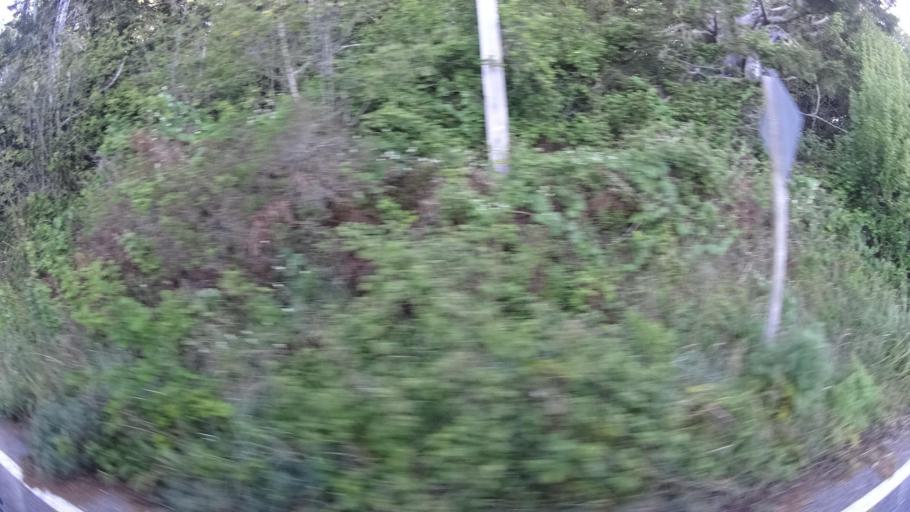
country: US
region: California
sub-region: Humboldt County
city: Westhaven-Moonstone
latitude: 41.0998
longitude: -124.1585
